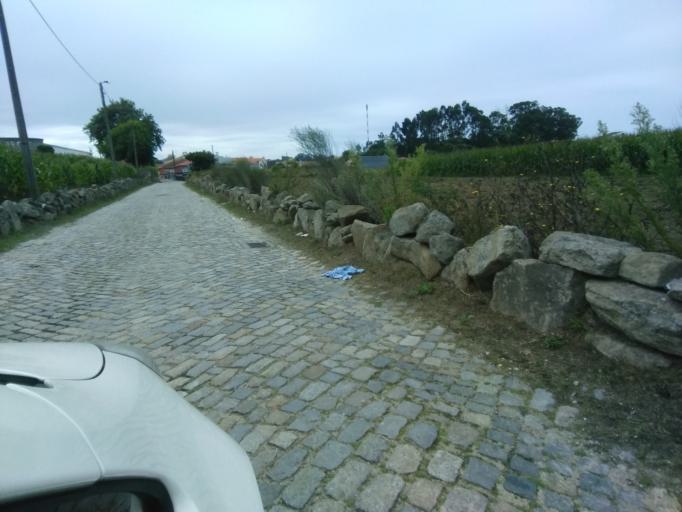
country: PT
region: Porto
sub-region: Matosinhos
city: Santa Cruz do Bispo
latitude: 41.2302
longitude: -8.7081
